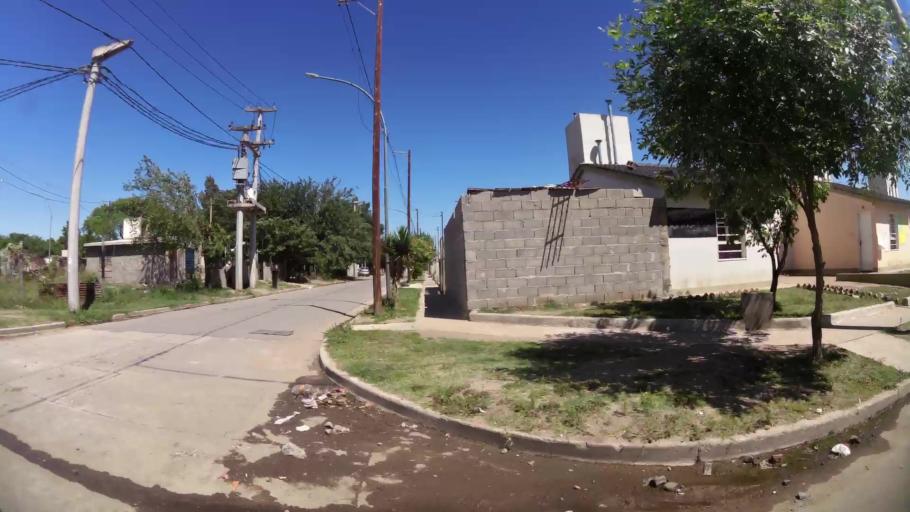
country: AR
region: Cordoba
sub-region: Departamento de Capital
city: Cordoba
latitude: -31.4086
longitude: -64.1355
